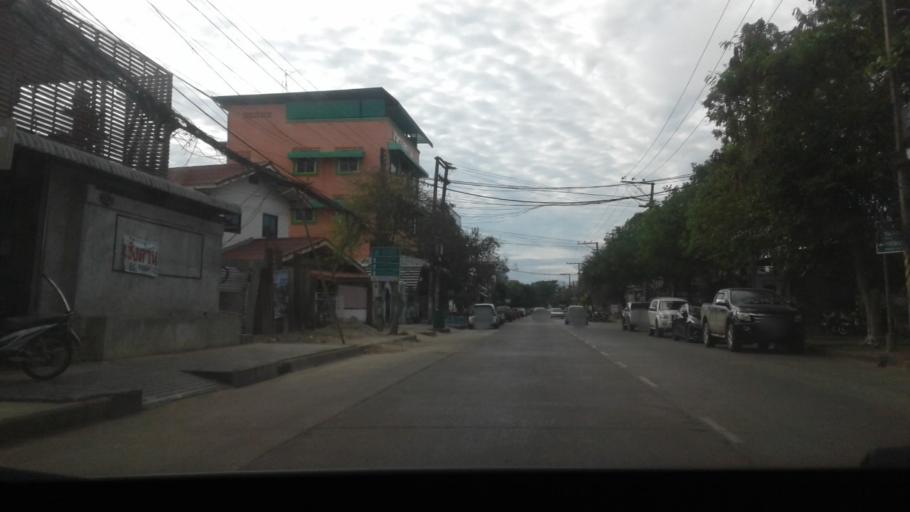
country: TH
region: Changwat Udon Thani
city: Udon Thani
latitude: 17.4167
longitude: 102.7959
